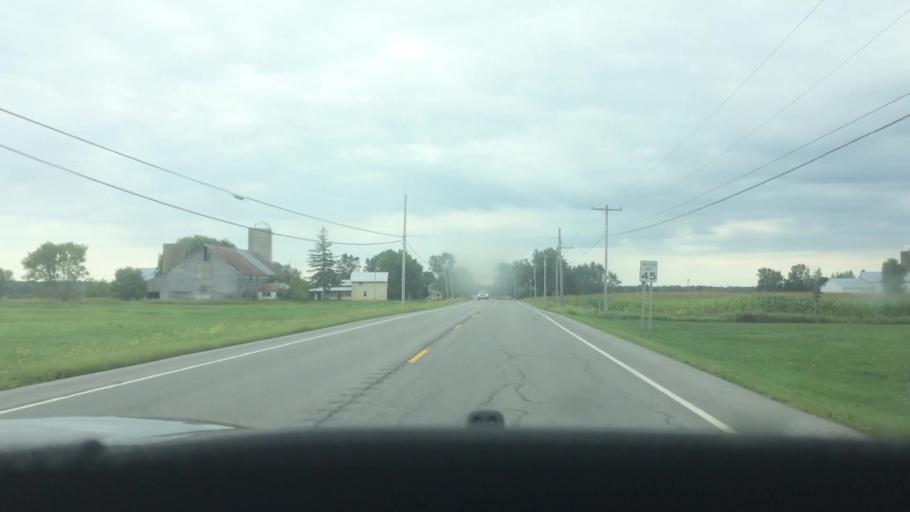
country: US
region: New York
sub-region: St. Lawrence County
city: Ogdensburg
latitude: 44.6736
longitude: -75.4738
